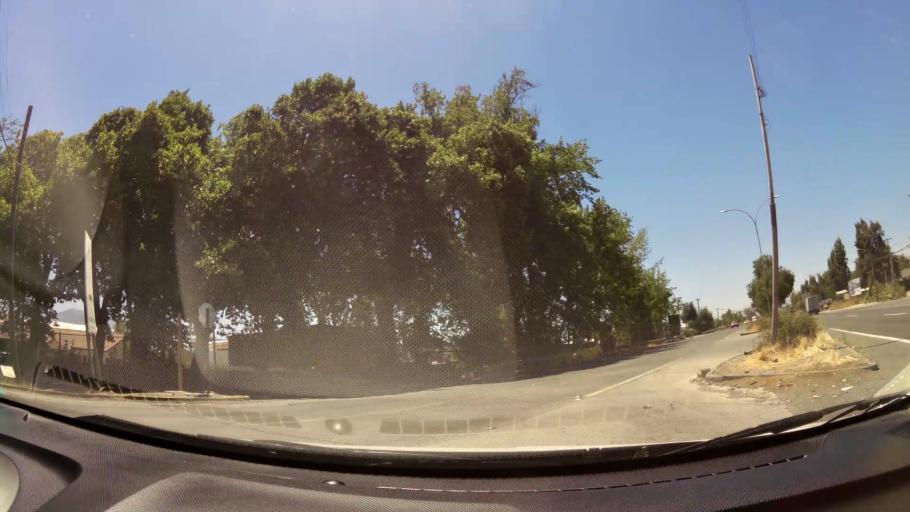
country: CL
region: O'Higgins
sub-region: Provincia de Cachapoal
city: Rancagua
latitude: -34.2241
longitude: -70.7799
